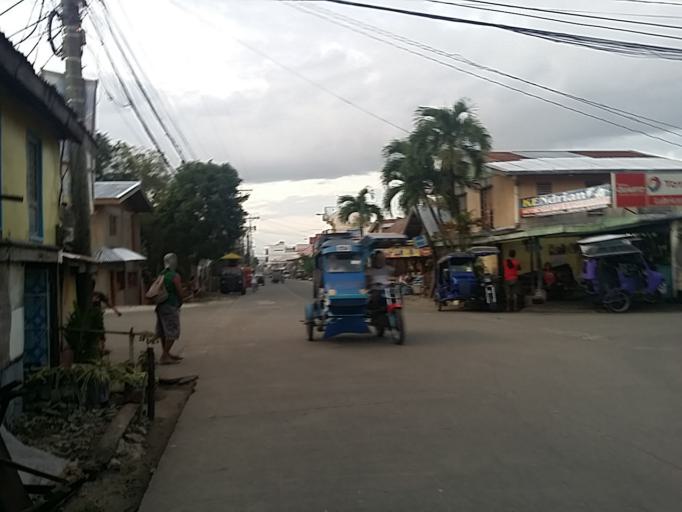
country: PH
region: Central Visayas
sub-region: Province of Cebu
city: Bogo
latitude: 11.0490
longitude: 124.0069
